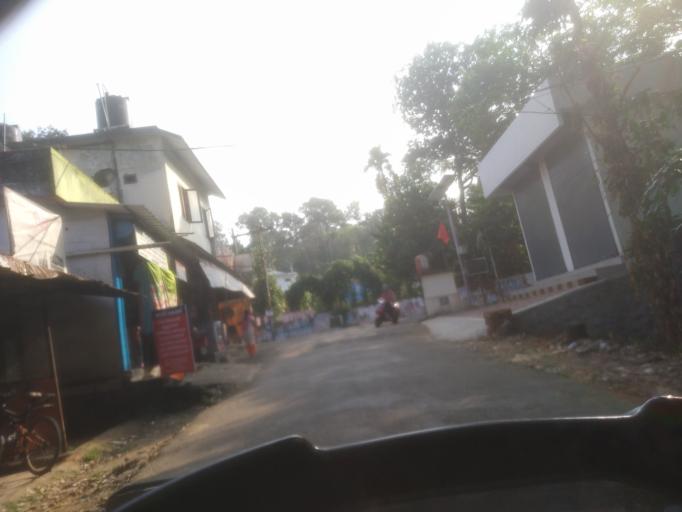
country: IN
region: Kerala
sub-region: Ernakulam
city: Piravam
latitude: 9.8392
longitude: 76.5248
